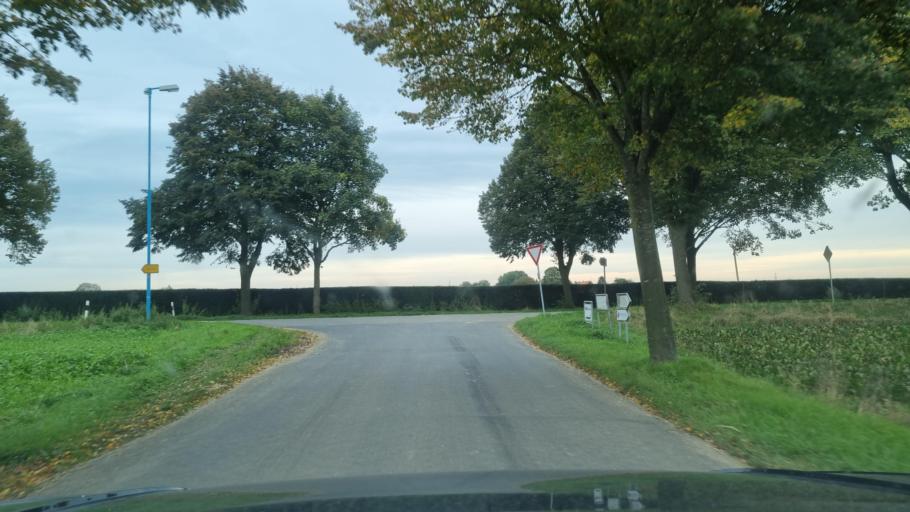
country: DE
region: North Rhine-Westphalia
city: Kalkar
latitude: 51.7145
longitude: 6.2527
